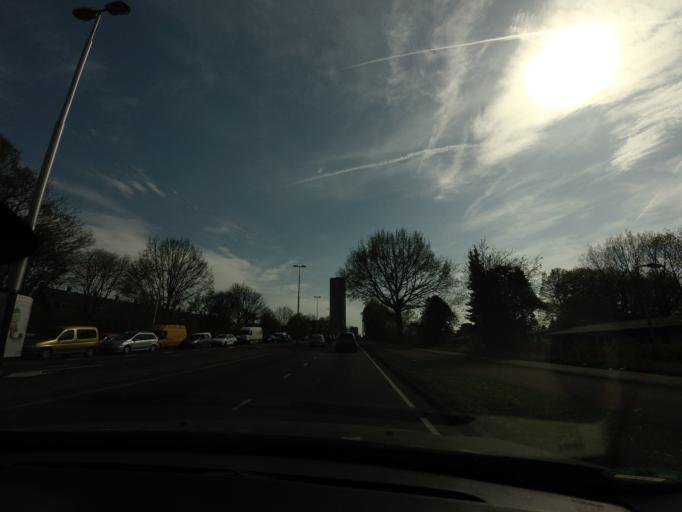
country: NL
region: North Brabant
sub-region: Gemeente Tilburg
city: Tilburg
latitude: 51.5660
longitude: 5.0656
